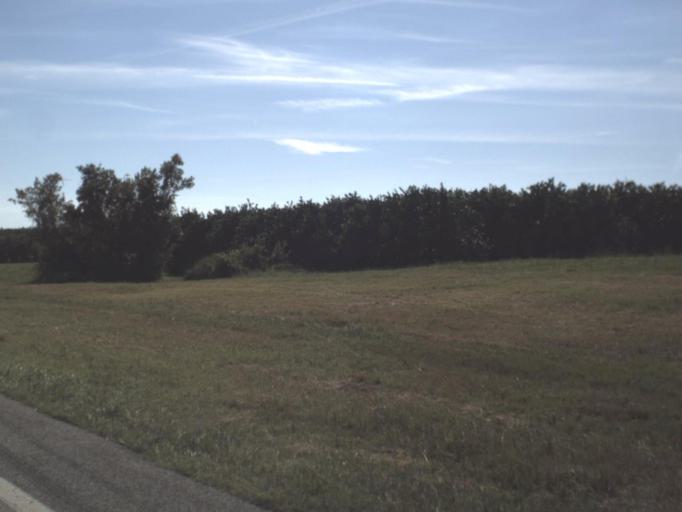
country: US
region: Florida
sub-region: Highlands County
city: Placid Lakes
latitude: 27.2021
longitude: -81.3288
